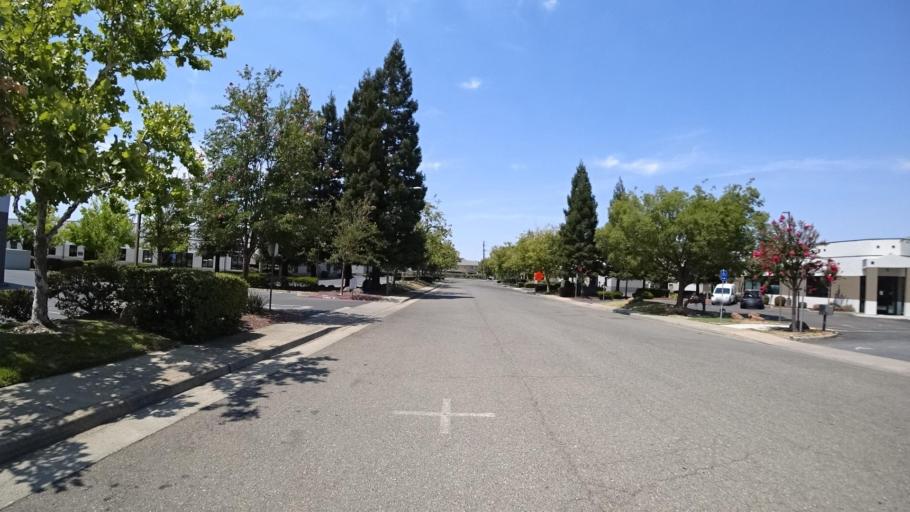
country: US
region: California
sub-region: Placer County
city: Rocklin
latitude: 38.8075
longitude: -121.2178
